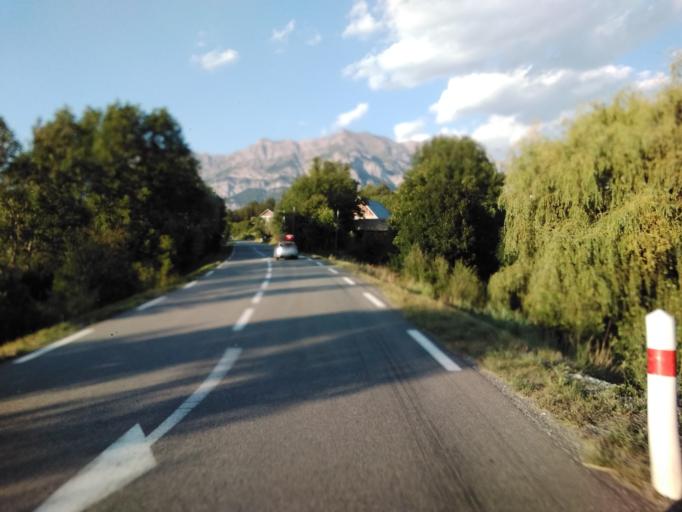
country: FR
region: Provence-Alpes-Cote d'Azur
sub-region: Departement des Alpes-de-Haute-Provence
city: Seyne-les-Alpes
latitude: 44.4436
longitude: 6.3515
